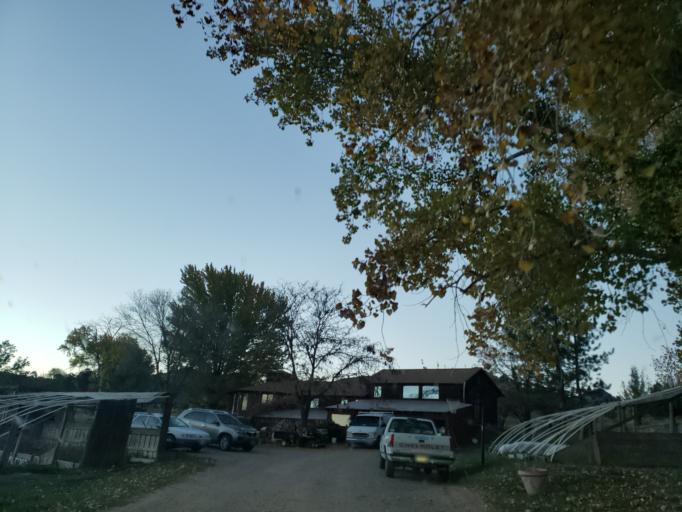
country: US
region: Colorado
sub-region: Garfield County
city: Silt
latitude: 39.5586
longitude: -107.6216
